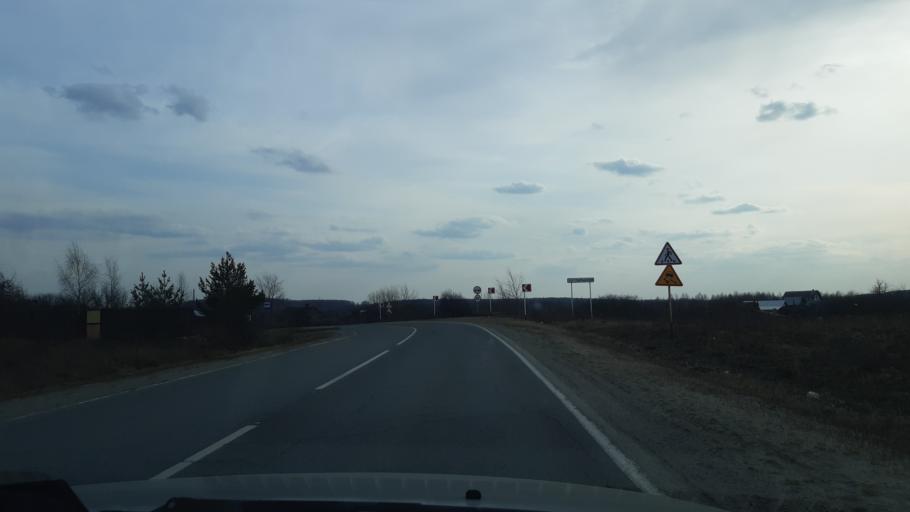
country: RU
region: Vladimir
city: Luknovo
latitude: 56.2158
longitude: 42.0302
